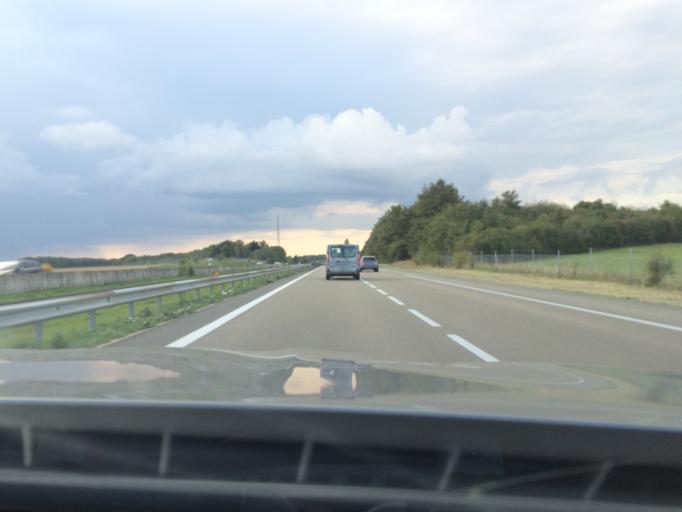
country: FR
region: Ile-de-France
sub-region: Departement de Seine-et-Marne
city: Egreville
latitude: 48.1567
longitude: 2.8903
